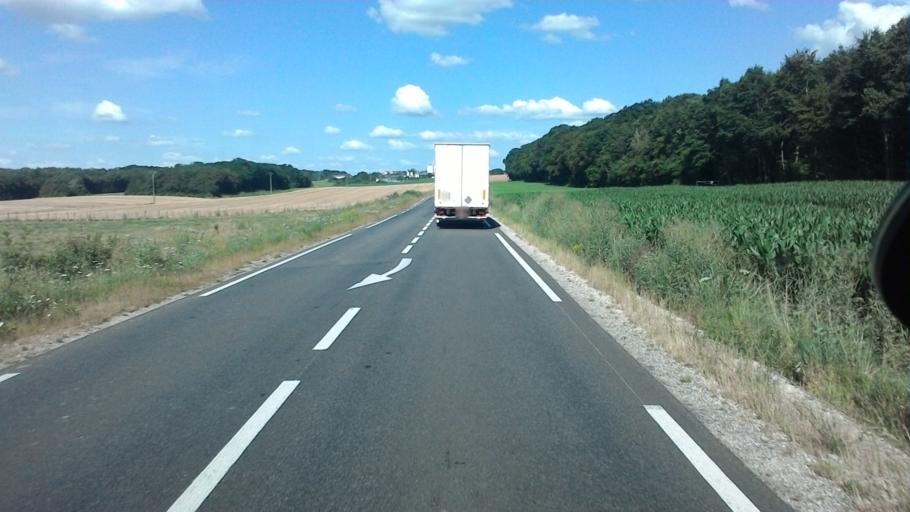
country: FR
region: Franche-Comte
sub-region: Departement de la Haute-Saone
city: Pesmes
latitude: 47.2921
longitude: 5.6058
